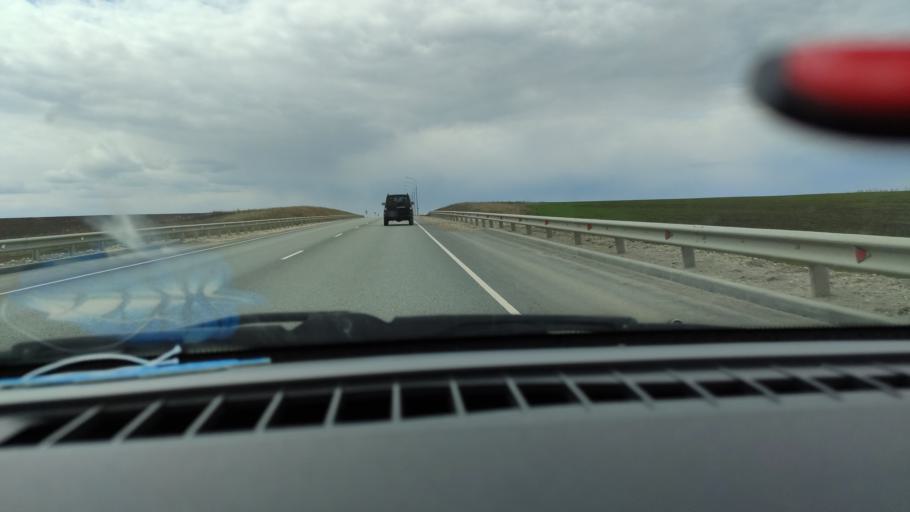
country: RU
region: Saratov
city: Yelshanka
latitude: 51.8307
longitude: 46.4369
